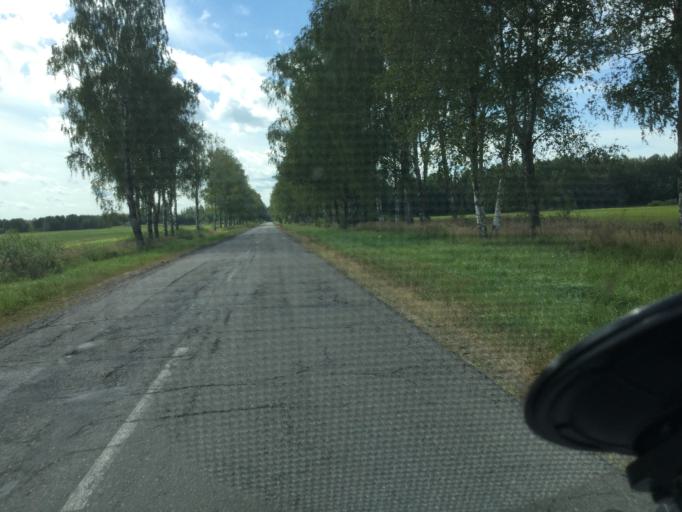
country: BY
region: Vitebsk
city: Chashniki
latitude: 55.3071
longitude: 29.4013
